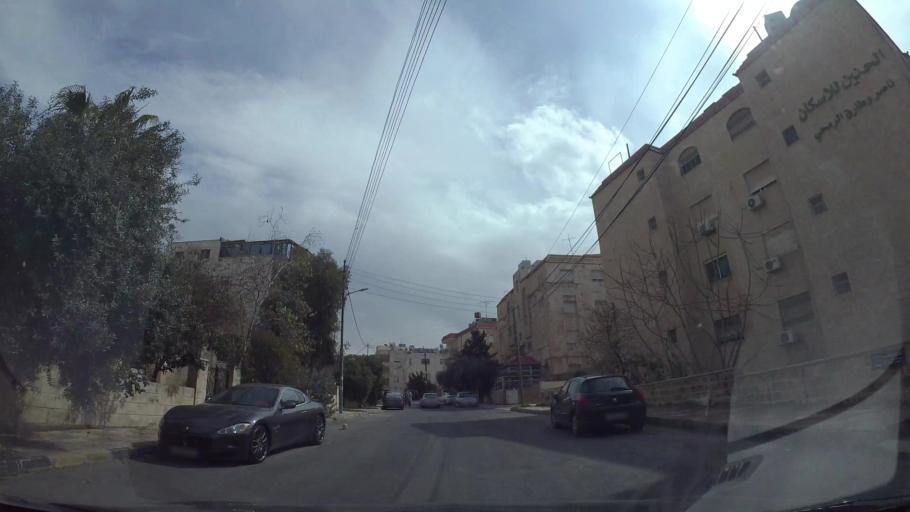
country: JO
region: Amman
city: Amman
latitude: 32.0014
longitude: 35.9365
